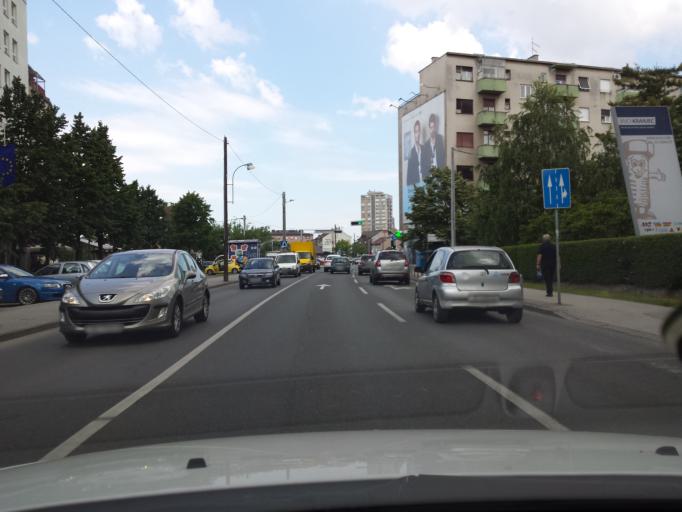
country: HR
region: Grad Zagreb
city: Zagreb - Centar
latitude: 45.7993
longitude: 15.9569
